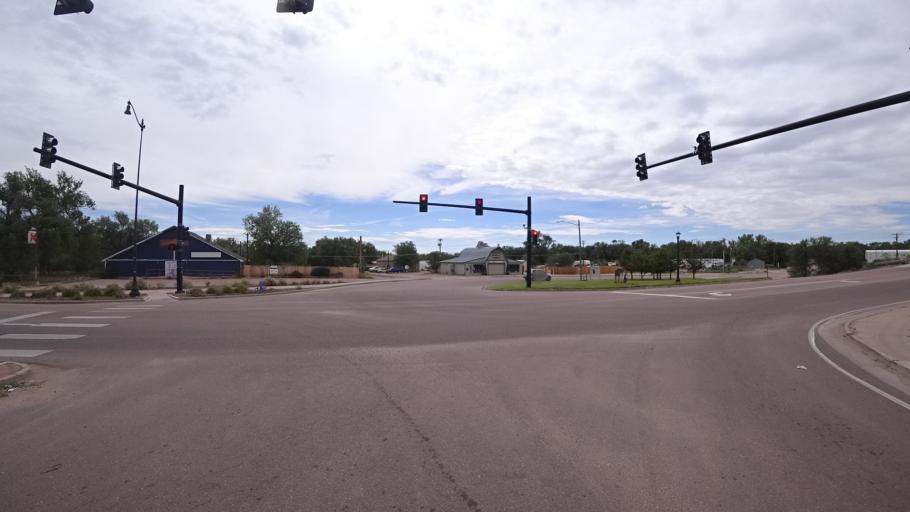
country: US
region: Colorado
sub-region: El Paso County
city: Fountain
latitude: 38.6755
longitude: -104.7061
